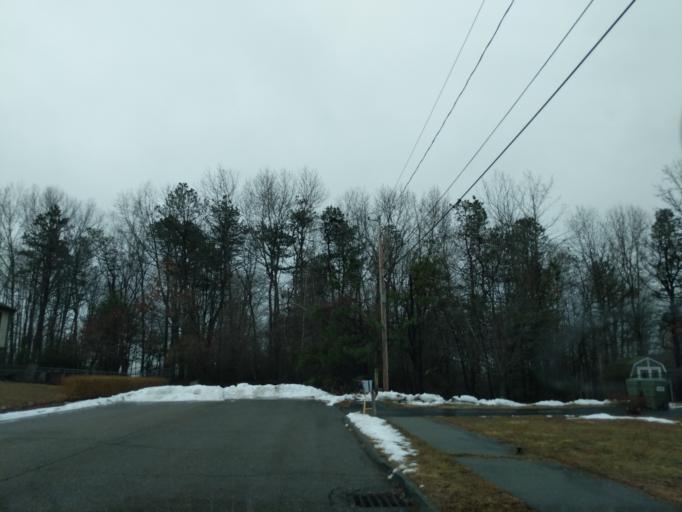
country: US
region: Massachusetts
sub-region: Worcester County
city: Webster
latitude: 42.0750
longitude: -71.8753
